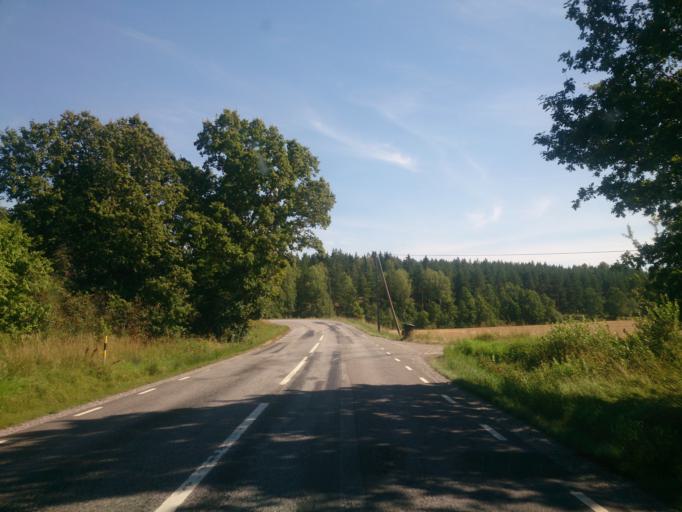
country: SE
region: OEstergoetland
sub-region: Norrkopings Kommun
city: Norrkoping
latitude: 58.4917
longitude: 16.1331
